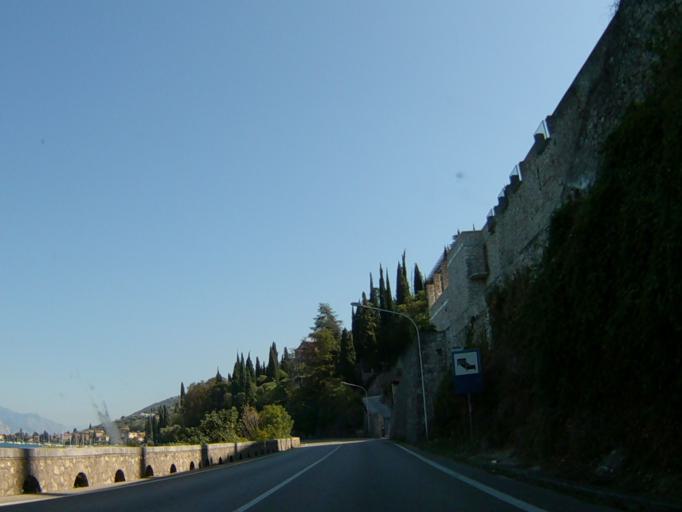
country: IT
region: Veneto
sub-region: Provincia di Verona
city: Torri del Benaco
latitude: 45.5935
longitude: 10.6807
